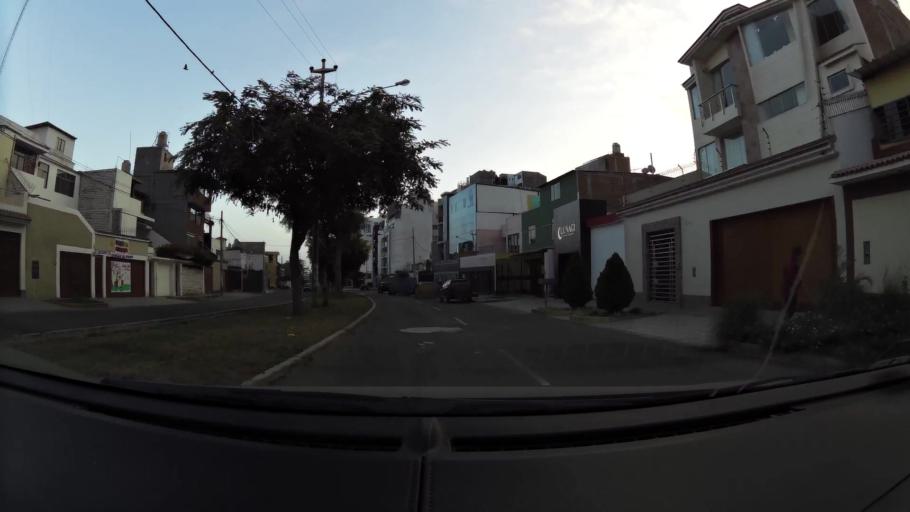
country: PE
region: La Libertad
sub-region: Provincia de Trujillo
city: Trujillo
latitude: -8.0954
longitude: -79.0328
